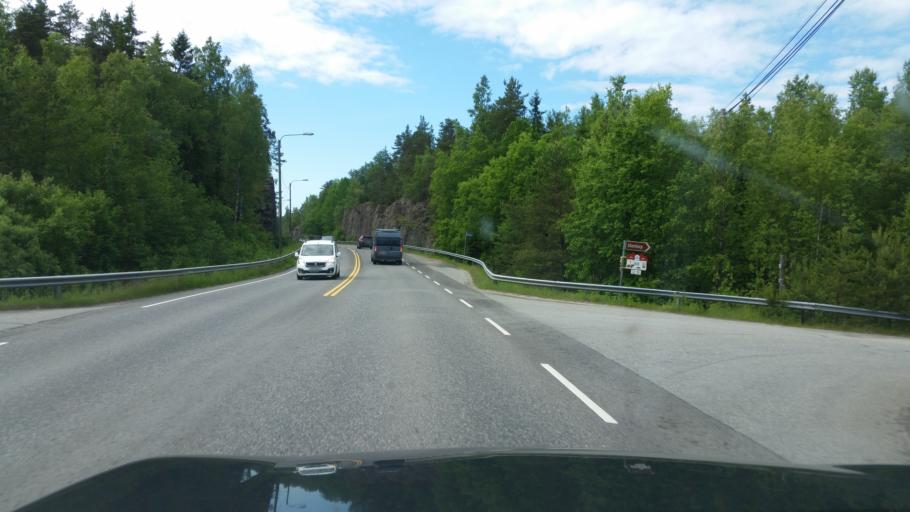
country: FI
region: Varsinais-Suomi
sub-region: Aboland-Turunmaa
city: Pargas
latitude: 60.3288
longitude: 22.3497
